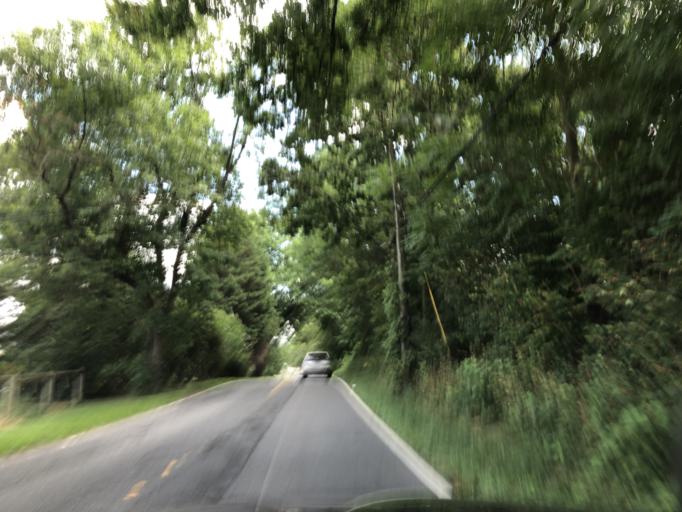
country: US
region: Maryland
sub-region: Frederick County
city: Clover Hill
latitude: 39.4301
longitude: -77.4440
